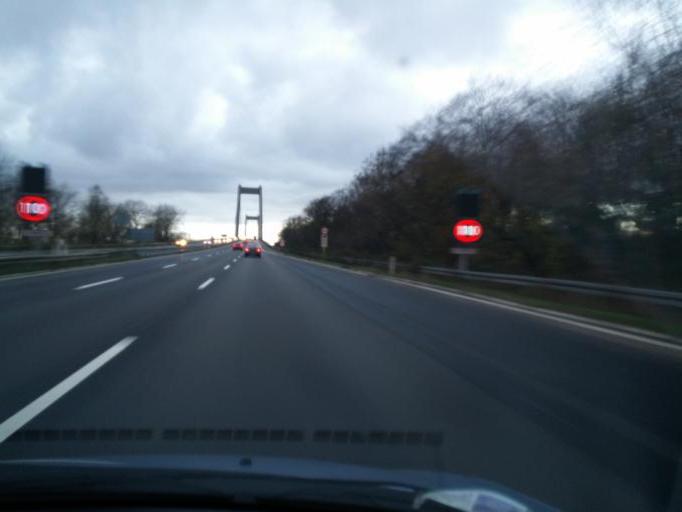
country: DK
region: South Denmark
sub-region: Middelfart Kommune
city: Strib
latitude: 55.5156
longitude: 9.7658
